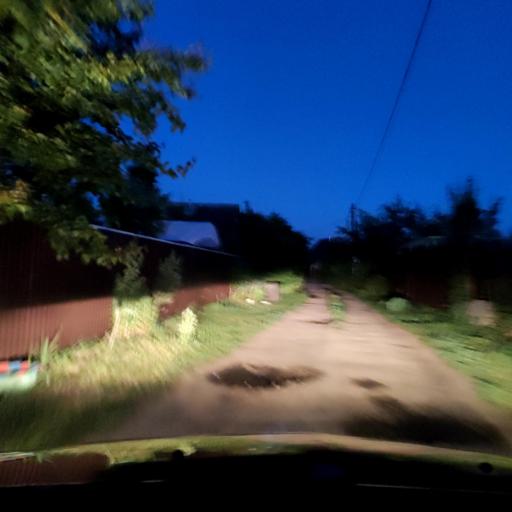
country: RU
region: Voronezj
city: Podgornoye
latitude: 51.8014
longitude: 39.2215
